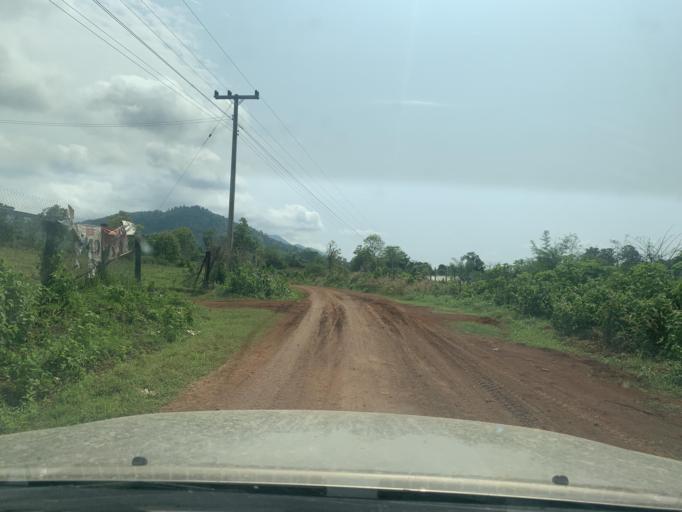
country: TH
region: Uttaradit
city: Ban Khok
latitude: 18.3669
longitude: 101.3964
